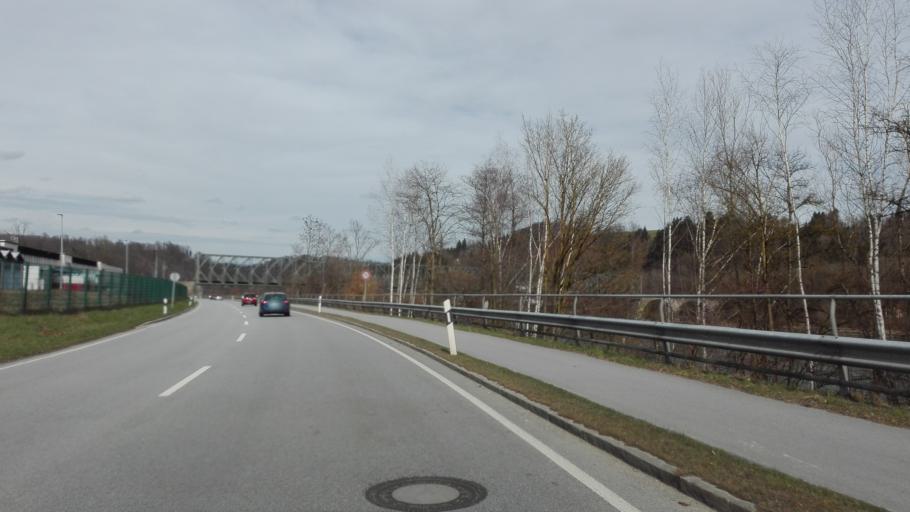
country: DE
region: Bavaria
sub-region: Lower Bavaria
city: Salzweg
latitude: 48.5783
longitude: 13.4969
